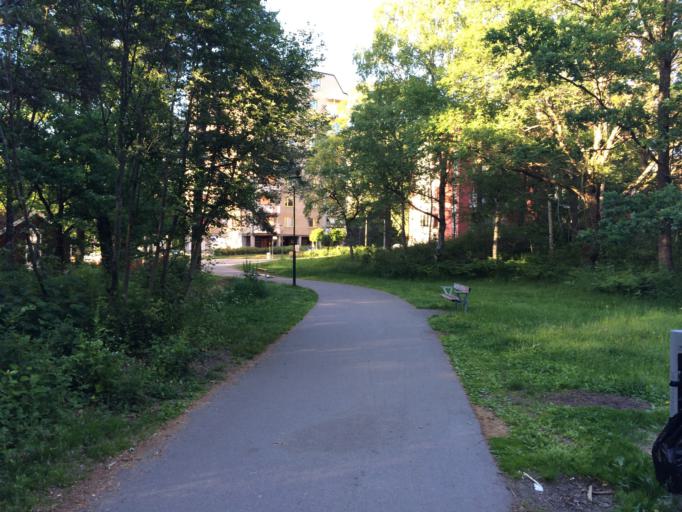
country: SE
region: Stockholm
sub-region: Huddinge Kommun
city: Segeltorp
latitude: 59.2947
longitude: 17.9723
